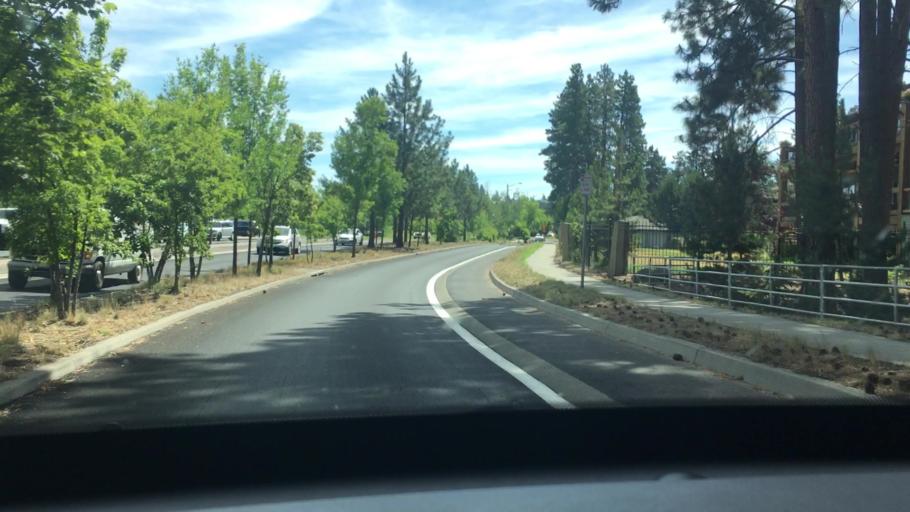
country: US
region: Oregon
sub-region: Deschutes County
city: Bend
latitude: 44.0406
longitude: -121.3246
